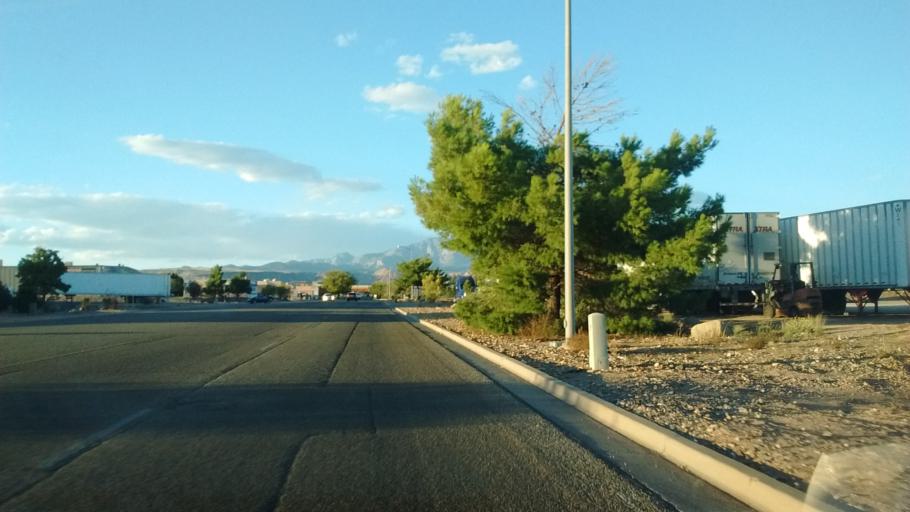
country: US
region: Utah
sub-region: Washington County
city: Washington
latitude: 37.1155
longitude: -113.5206
